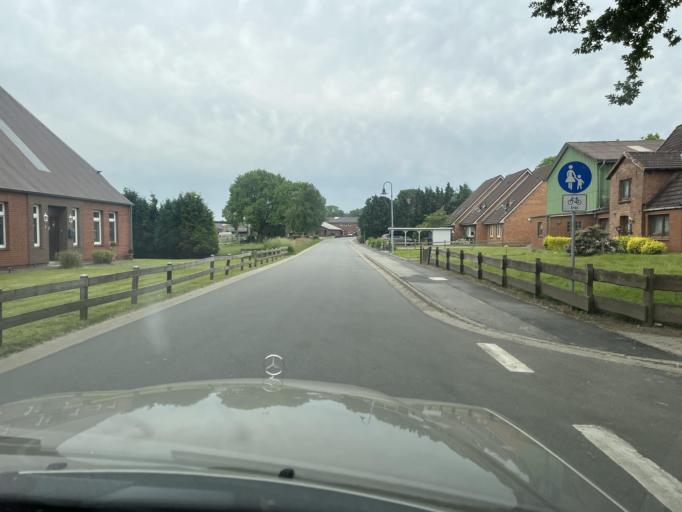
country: DE
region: Schleswig-Holstein
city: Hemmingstedt
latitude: 54.1532
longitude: 9.0920
